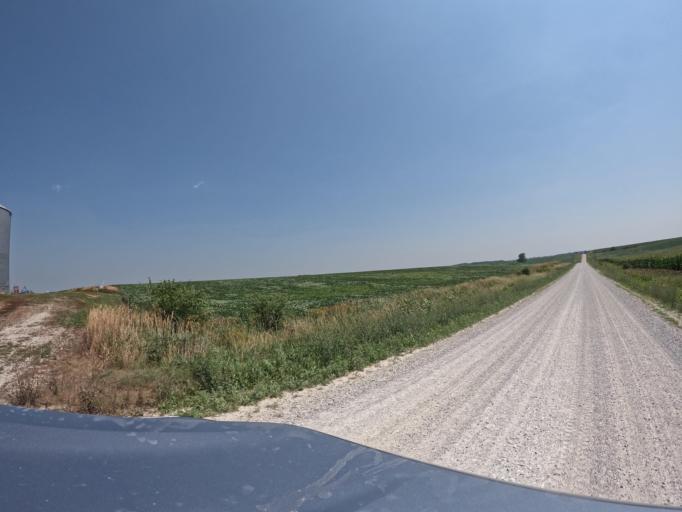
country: US
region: Iowa
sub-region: Keokuk County
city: Sigourney
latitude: 41.3343
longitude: -92.2386
